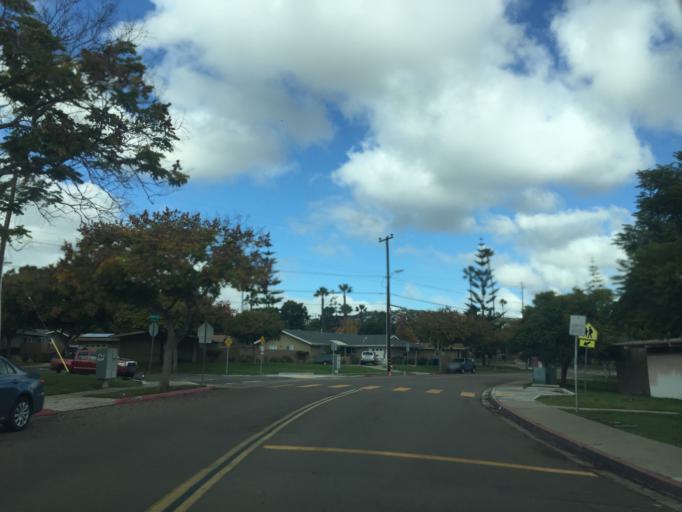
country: US
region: California
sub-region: San Diego County
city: La Jolla
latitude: 32.8020
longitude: -117.2258
